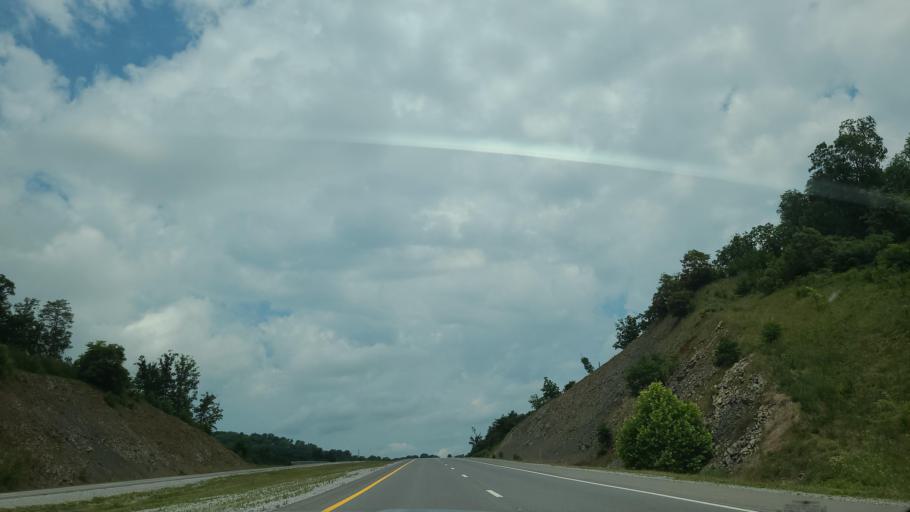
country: US
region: Tennessee
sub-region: Jefferson County
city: White Pine
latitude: 36.1348
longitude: -83.3386
